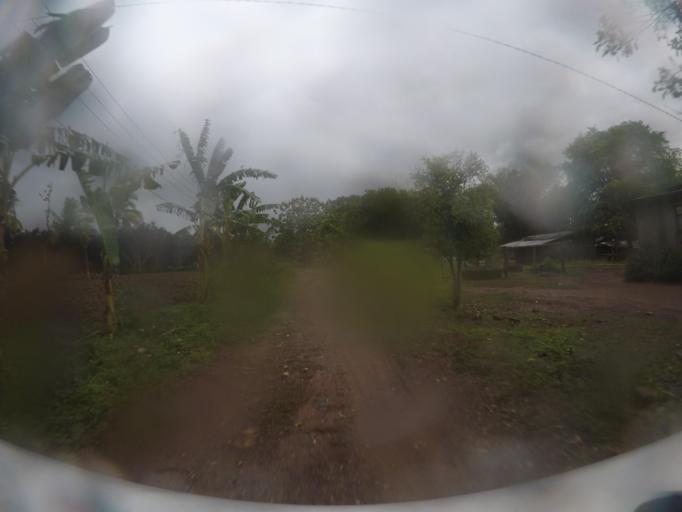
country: TL
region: Bobonaro
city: Maliana
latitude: -8.9656
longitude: 125.2153
